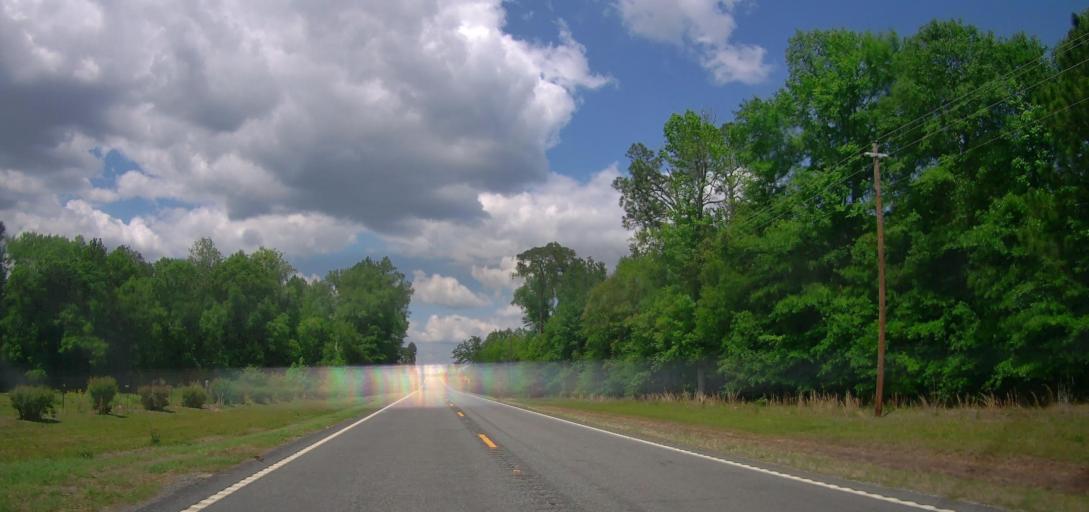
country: US
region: Georgia
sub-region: Treutlen County
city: Soperton
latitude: 32.4063
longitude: -82.6065
